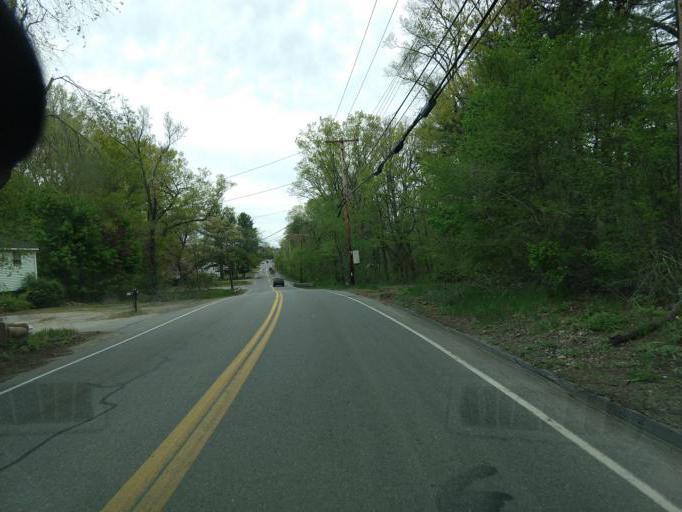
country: US
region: Massachusetts
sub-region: Middlesex County
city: Tewksbury
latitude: 42.5952
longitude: -71.1963
